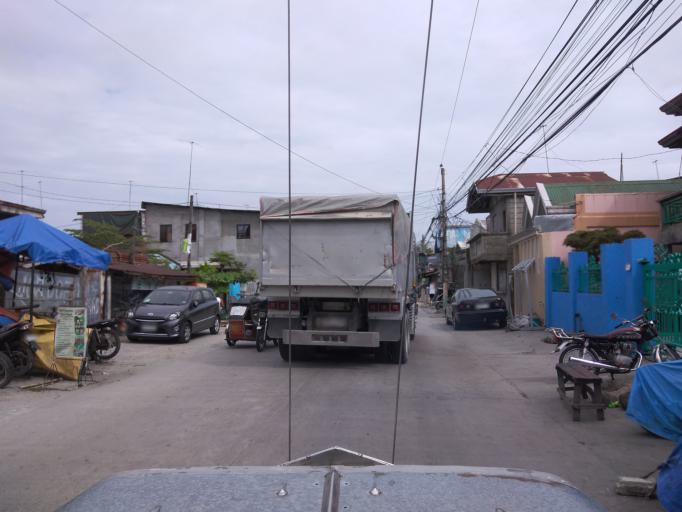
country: PH
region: Central Luzon
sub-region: Province of Pampanga
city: Sexmoan
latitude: 14.9410
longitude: 120.6213
